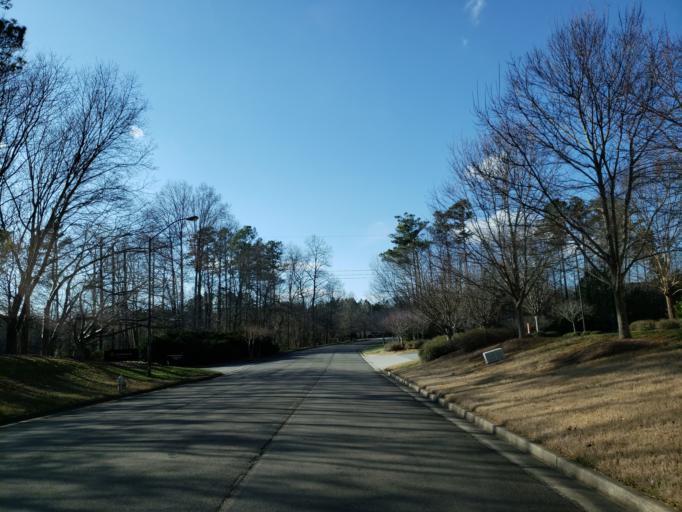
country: US
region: Georgia
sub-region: Cobb County
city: Marietta
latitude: 33.9900
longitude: -84.5211
